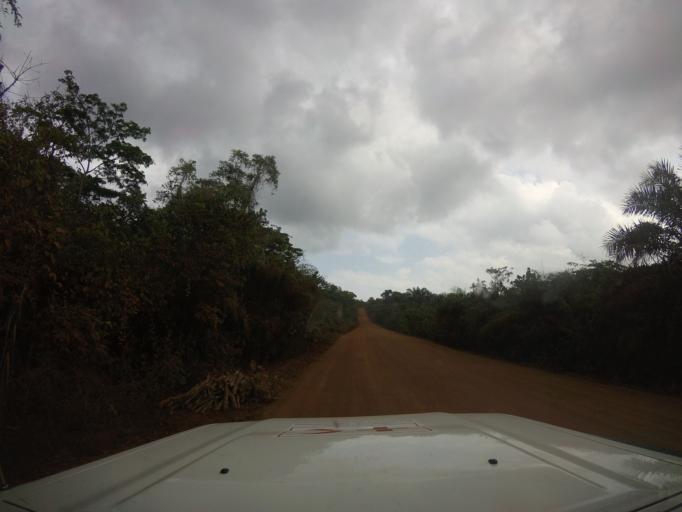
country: LR
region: Grand Cape Mount
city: Robertsport
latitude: 6.7274
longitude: -11.3384
